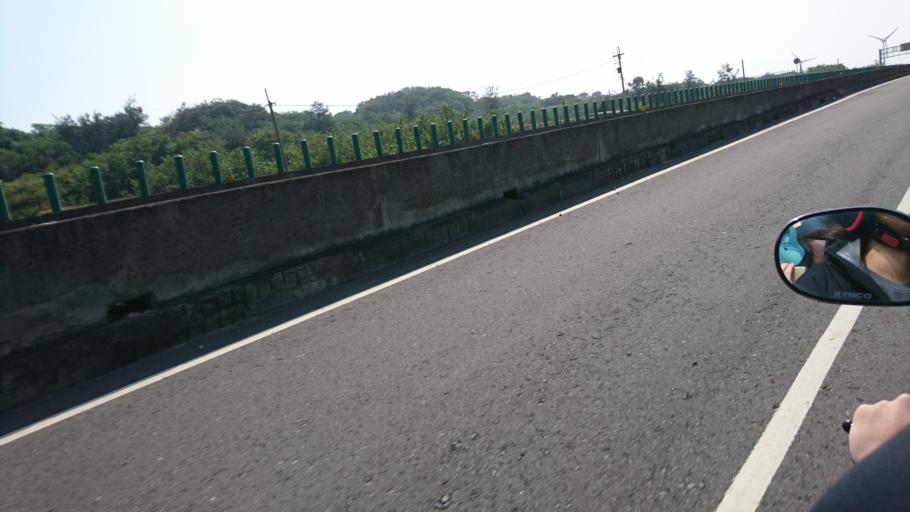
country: TW
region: Taiwan
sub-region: Hsinchu
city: Hsinchu
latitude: 24.7290
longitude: 120.8747
